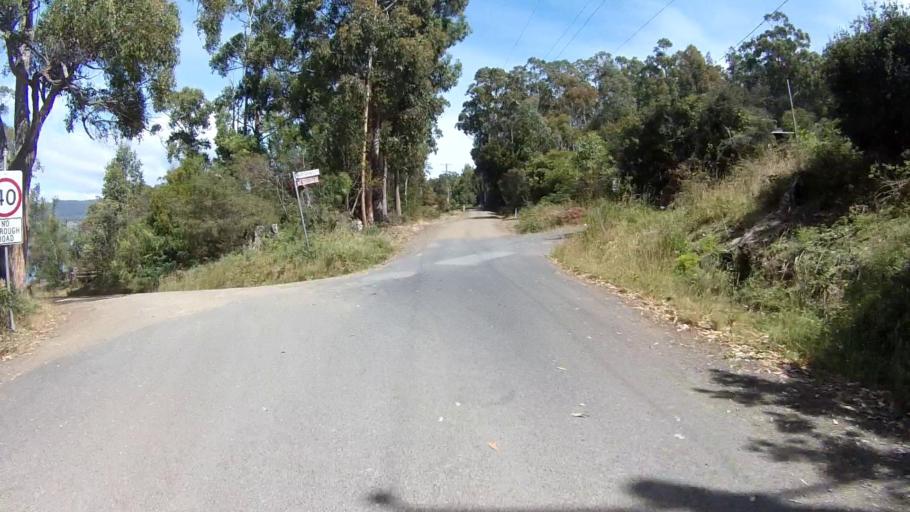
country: AU
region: Tasmania
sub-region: Huon Valley
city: Cygnet
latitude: -43.2447
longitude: 147.1003
